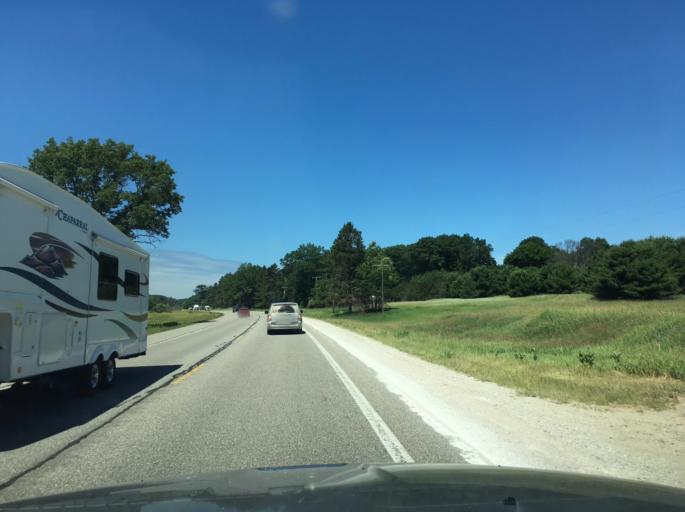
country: US
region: Michigan
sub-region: Osceola County
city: Reed City
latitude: 43.8921
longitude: -85.6566
